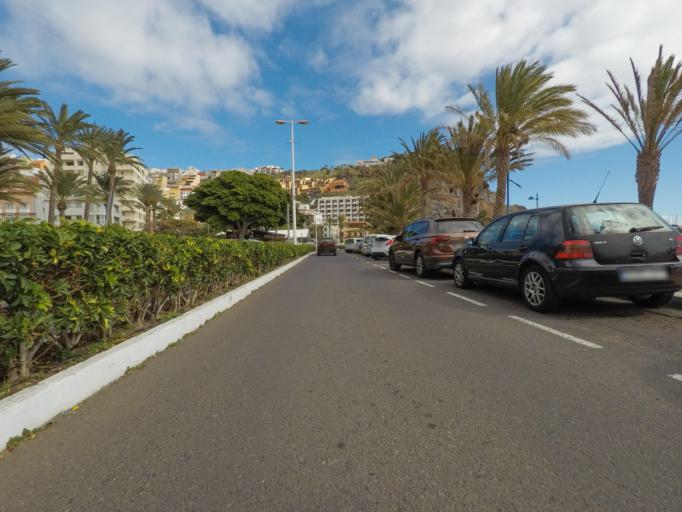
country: ES
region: Canary Islands
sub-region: Provincia de Santa Cruz de Tenerife
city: San Sebastian de la Gomera
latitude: 28.0897
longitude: -17.1113
